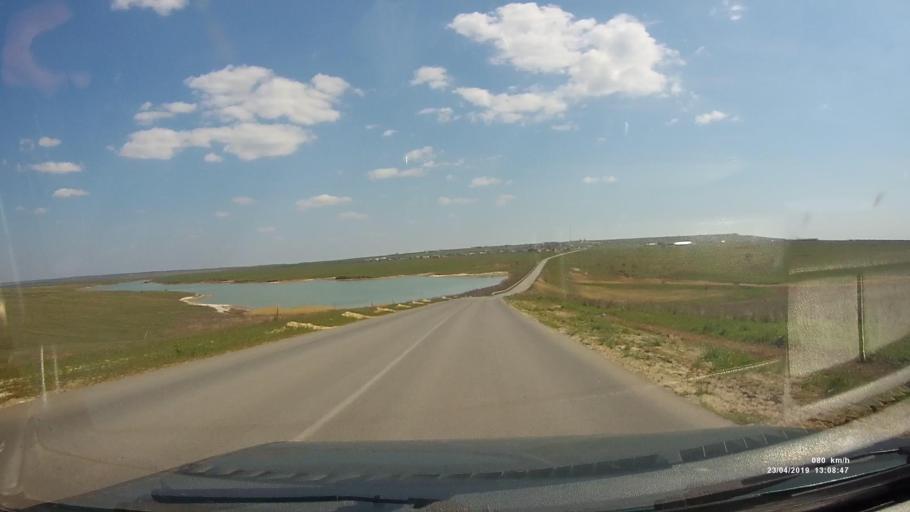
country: RU
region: Kalmykiya
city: Yashalta
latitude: 46.5804
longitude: 42.7803
